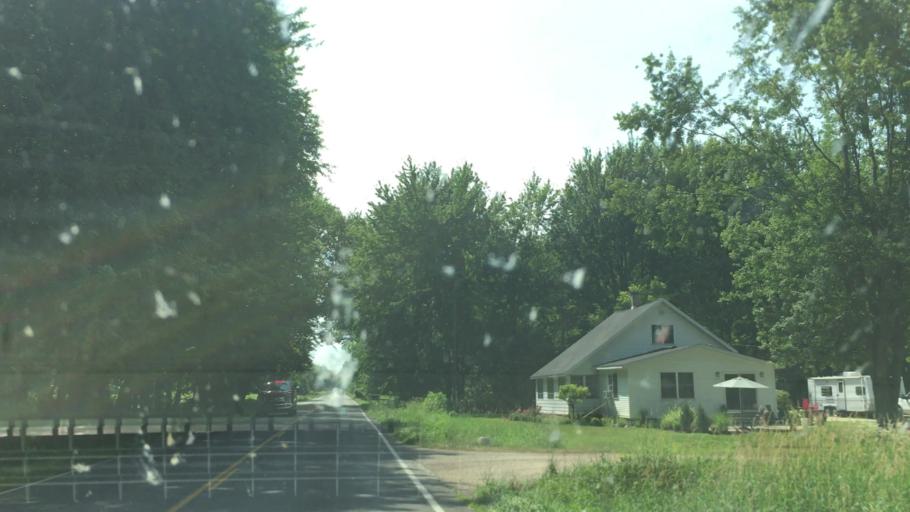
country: US
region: Michigan
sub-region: Kent County
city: Byron Center
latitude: 42.7829
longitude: -85.7145
